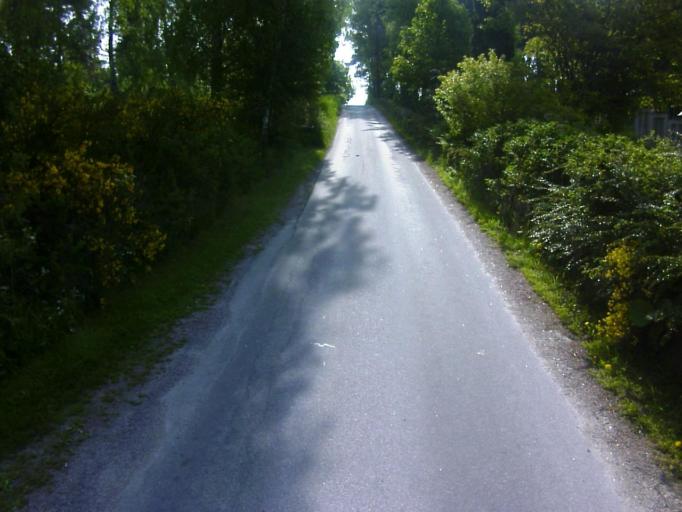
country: SE
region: Blekinge
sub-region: Karlshamns Kommun
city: Morrum
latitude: 56.0498
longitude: 14.7475
